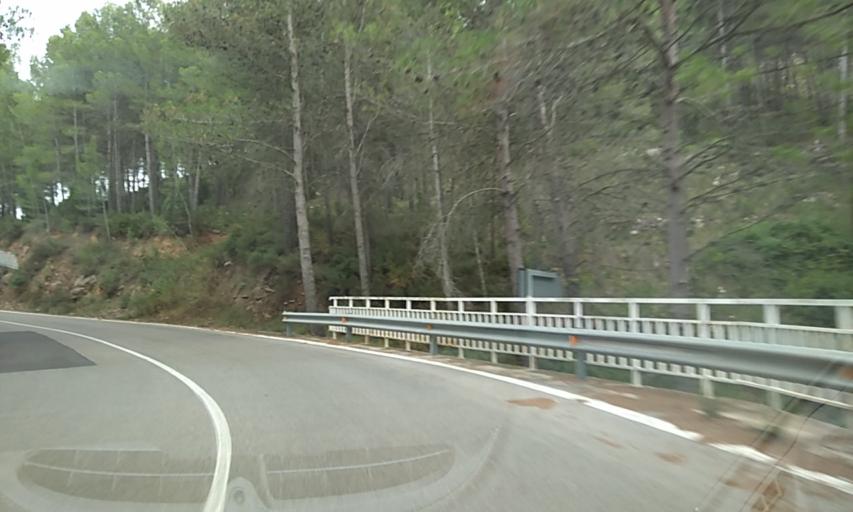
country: ES
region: Valencia
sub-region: Provincia de Castello
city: Puebla de Arenoso
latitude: 40.0871
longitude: -0.5580
